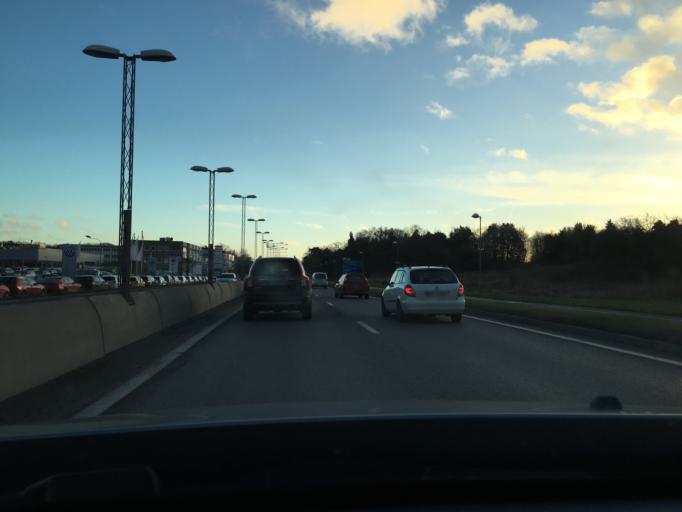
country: SE
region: Stockholm
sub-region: Stockholms Kommun
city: Bromma
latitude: 59.3484
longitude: 17.9571
